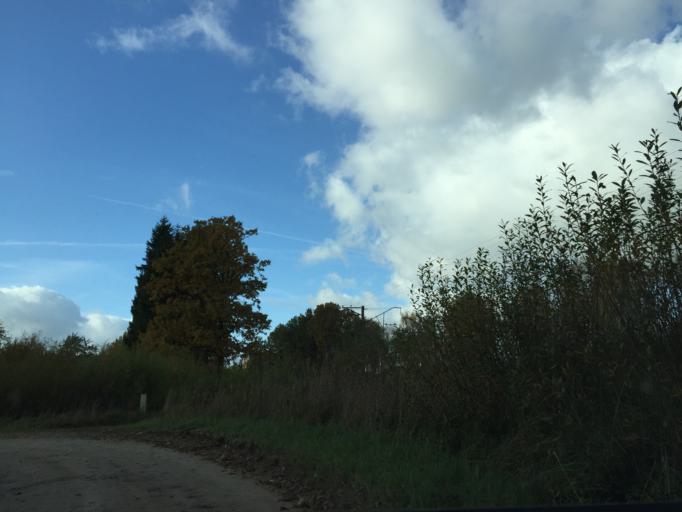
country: LV
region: Lielvarde
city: Lielvarde
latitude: 56.7037
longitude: 24.8860
